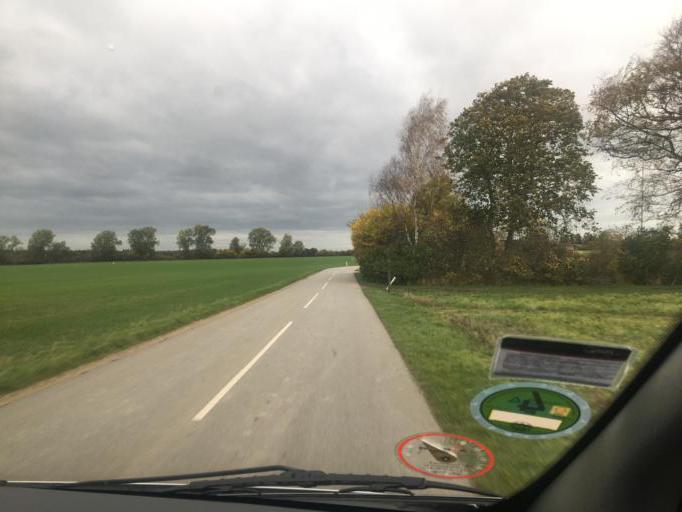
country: DK
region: Zealand
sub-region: Koge Kommune
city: Bjaeverskov
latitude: 55.4208
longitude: 11.9827
